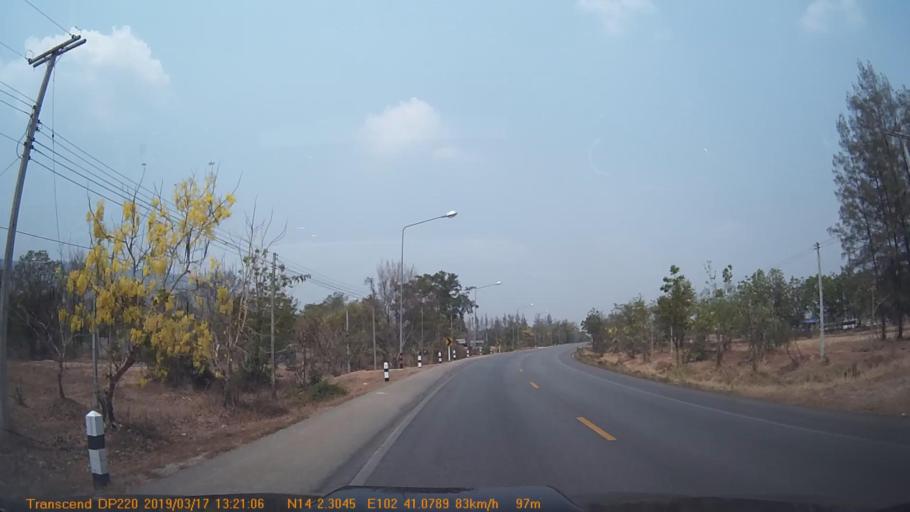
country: TH
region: Sa Kaeo
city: Ta Phraya
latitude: 14.0387
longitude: 102.6847
